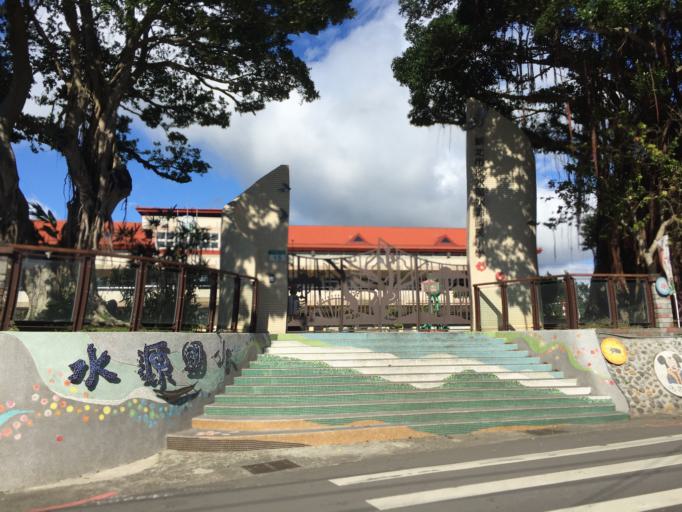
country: TW
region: Taipei
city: Taipei
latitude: 25.1857
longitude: 121.4765
